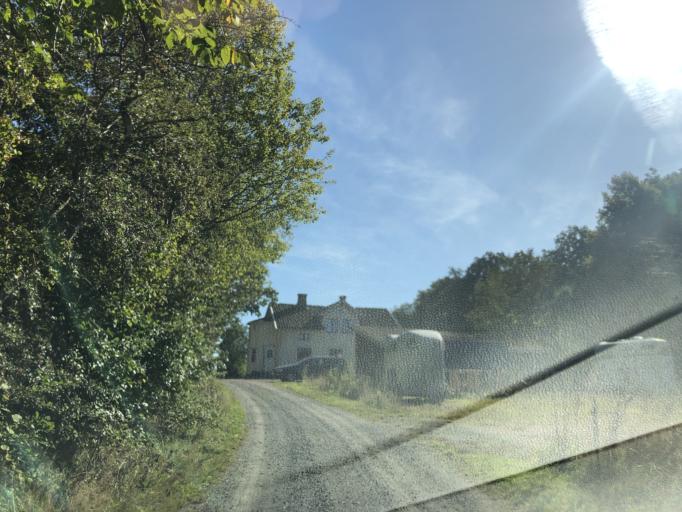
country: SE
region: Vaestra Goetaland
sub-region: Goteborg
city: Goeteborg
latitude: 57.7707
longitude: 11.9238
